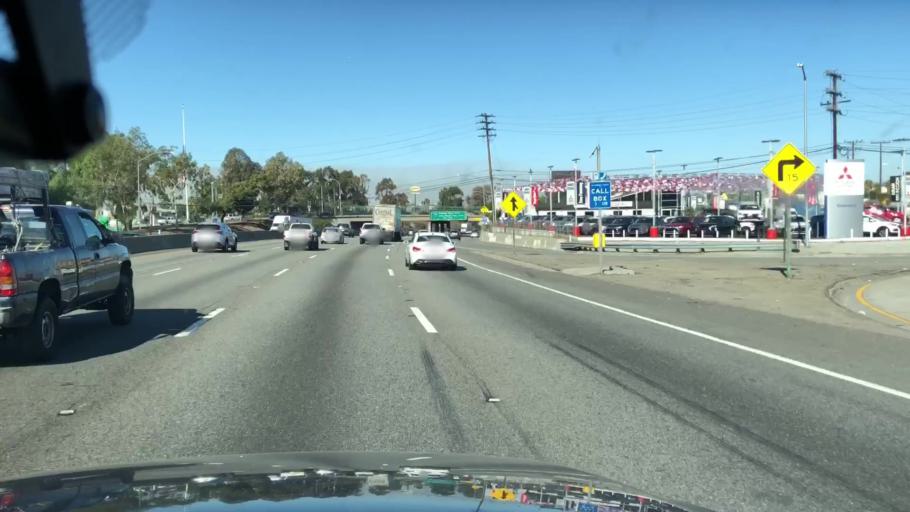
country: US
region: California
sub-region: Los Angeles County
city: Commerce
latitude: 34.0074
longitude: -118.1567
